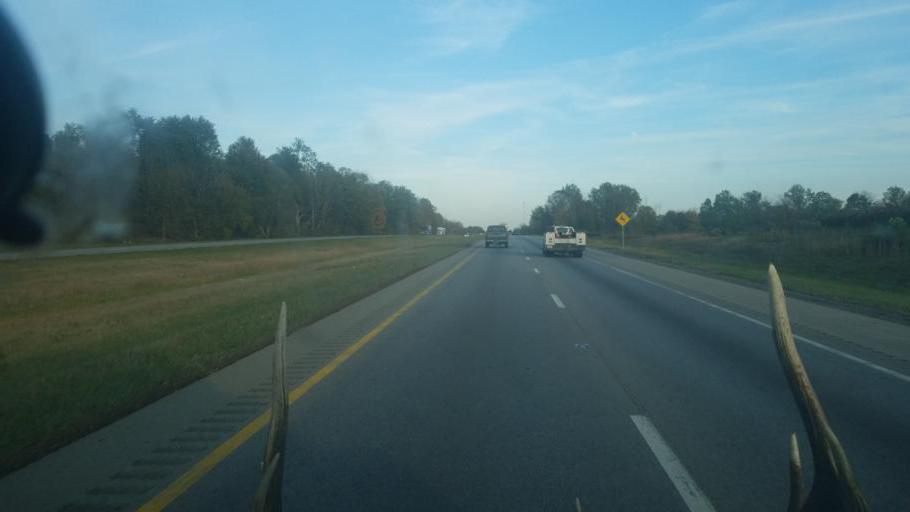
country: US
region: Ohio
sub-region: Licking County
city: Etna
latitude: 39.9467
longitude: -82.6428
